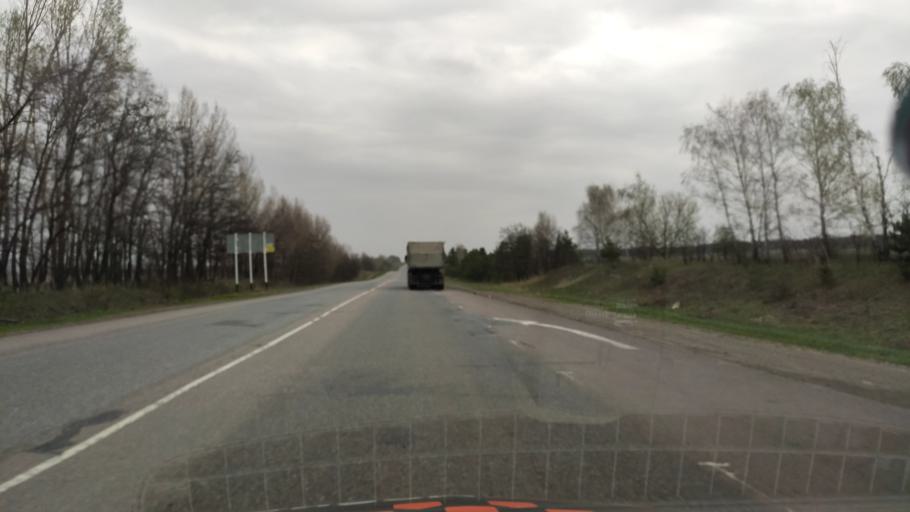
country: RU
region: Belgorod
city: Staryy Oskol
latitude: 51.4383
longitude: 37.9057
